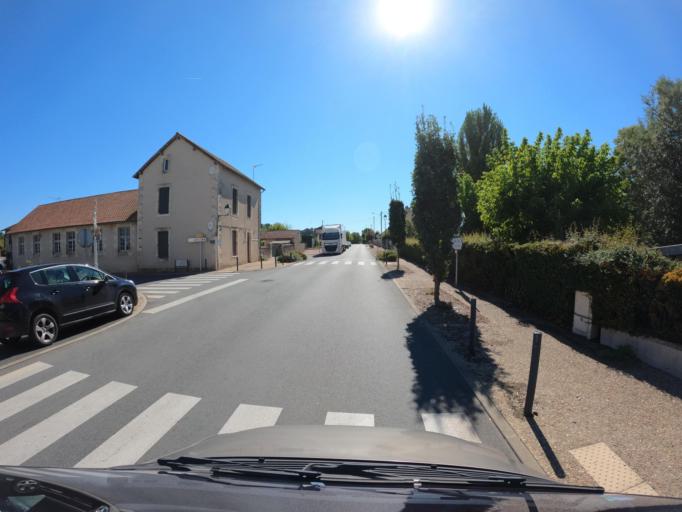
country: FR
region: Poitou-Charentes
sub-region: Departement de la Vienne
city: Lathus-Saint-Remy
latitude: 46.3317
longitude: 0.9625
